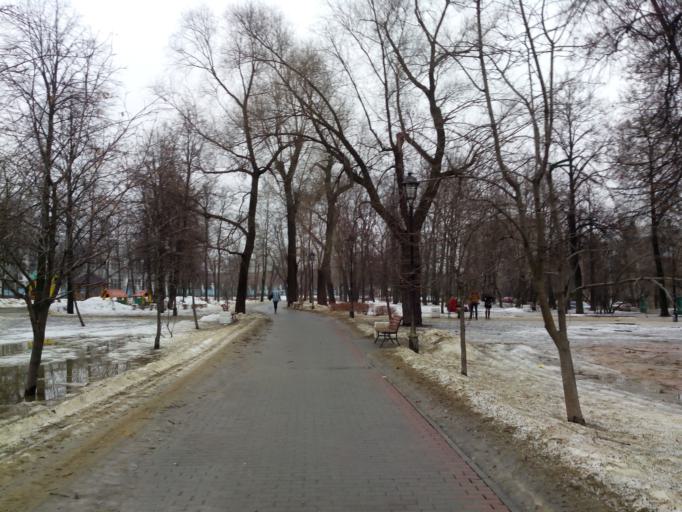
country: RU
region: Moscow
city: Lefortovo
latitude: 55.7783
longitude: 37.7169
